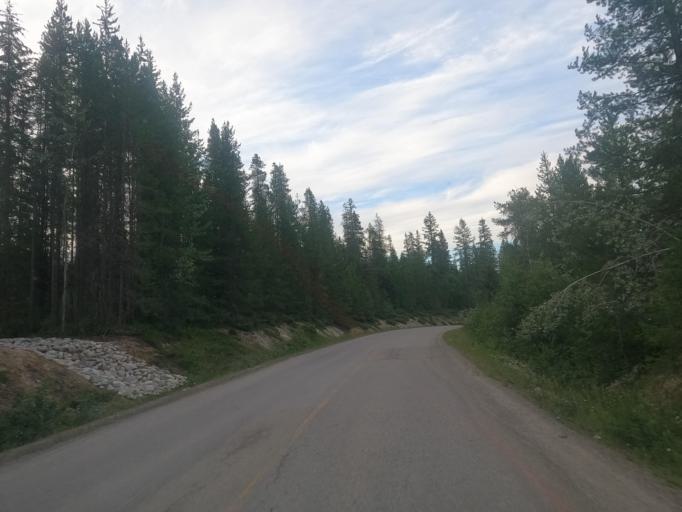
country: CA
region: British Columbia
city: Golden
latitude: 51.4294
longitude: -117.0445
